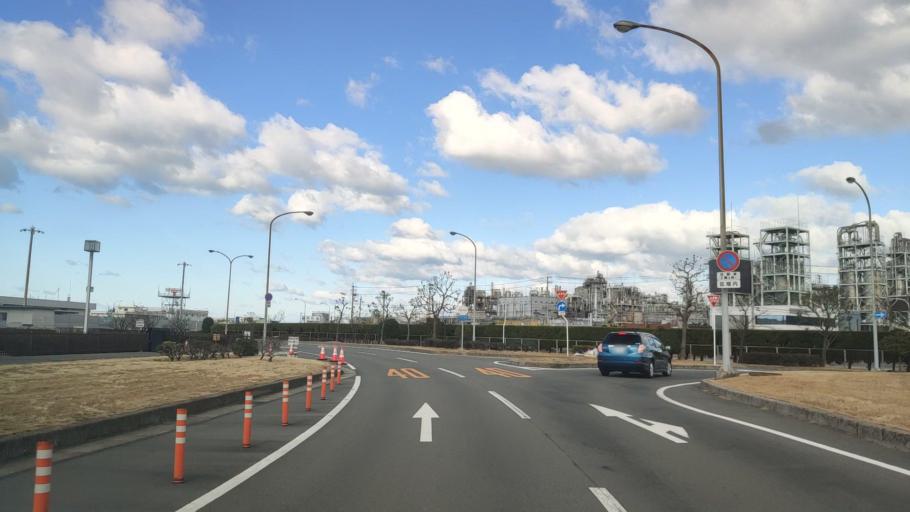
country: JP
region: Ehime
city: Masaki-cho
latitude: 33.8299
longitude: 132.7036
